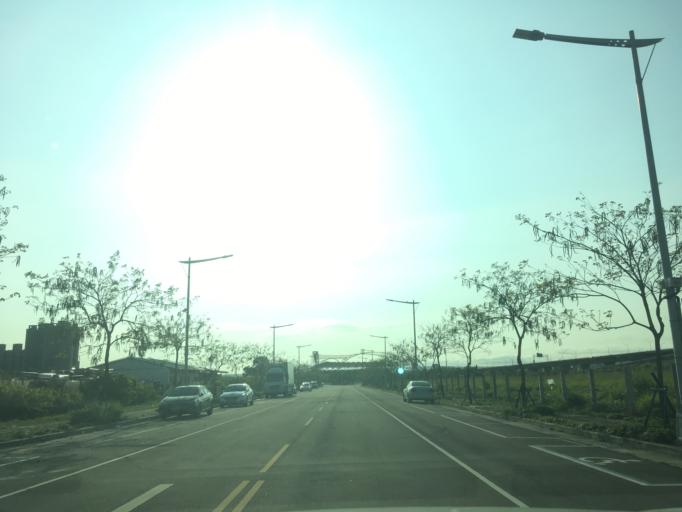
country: TW
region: Taiwan
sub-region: Taichung City
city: Taichung
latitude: 24.1995
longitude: 120.6931
